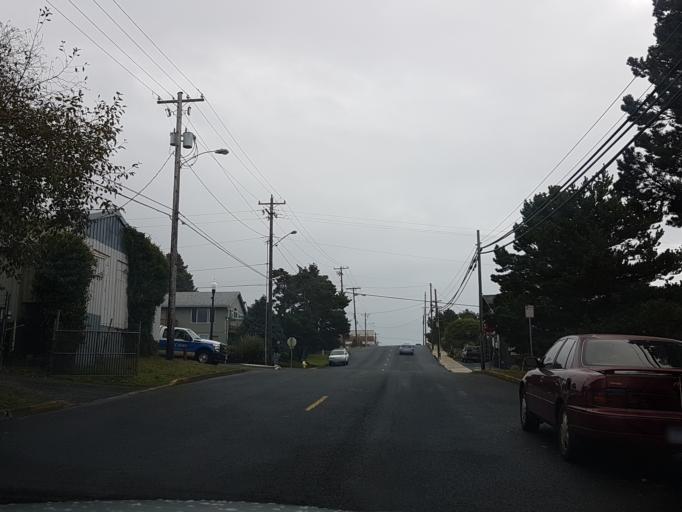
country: US
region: Oregon
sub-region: Lincoln County
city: Newport
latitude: 44.6389
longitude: -124.0557
